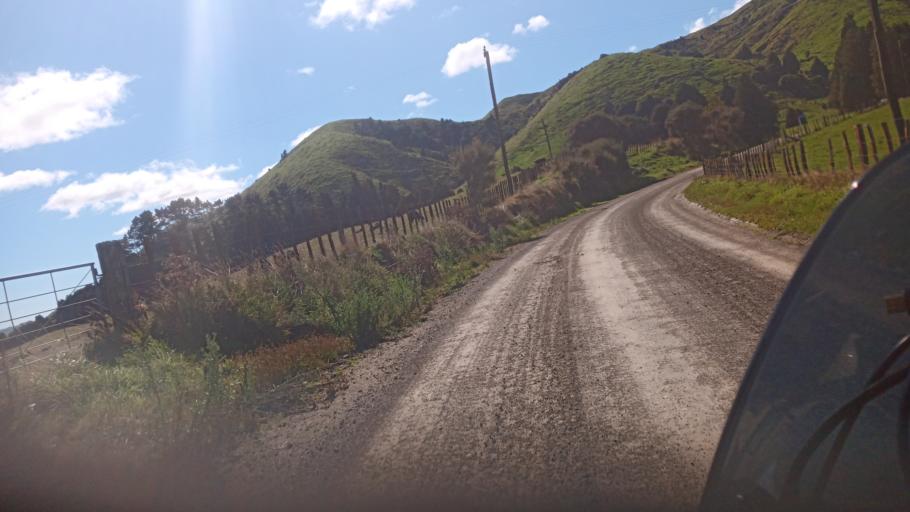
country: NZ
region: Bay of Plenty
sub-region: Opotiki District
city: Opotiki
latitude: -38.3154
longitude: 177.5693
